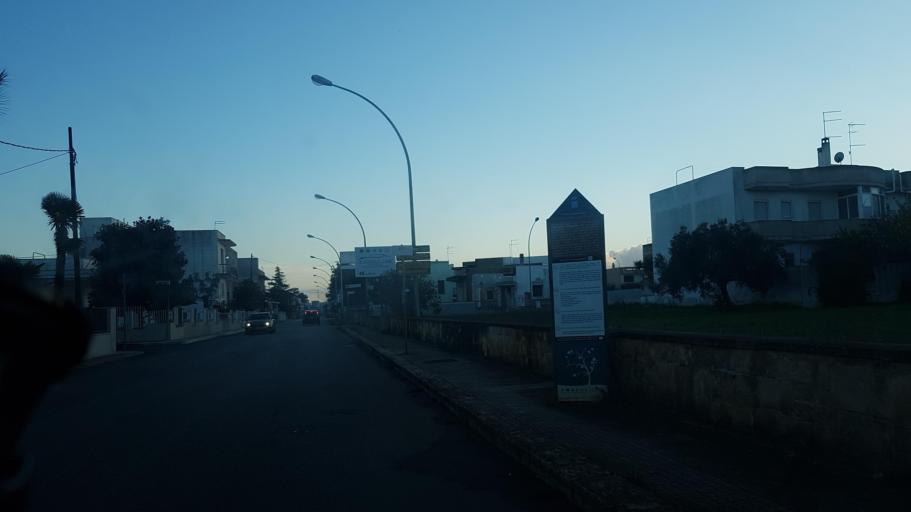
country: IT
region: Apulia
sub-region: Provincia di Brindisi
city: San Michele Salentino
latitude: 40.6369
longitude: 17.6320
